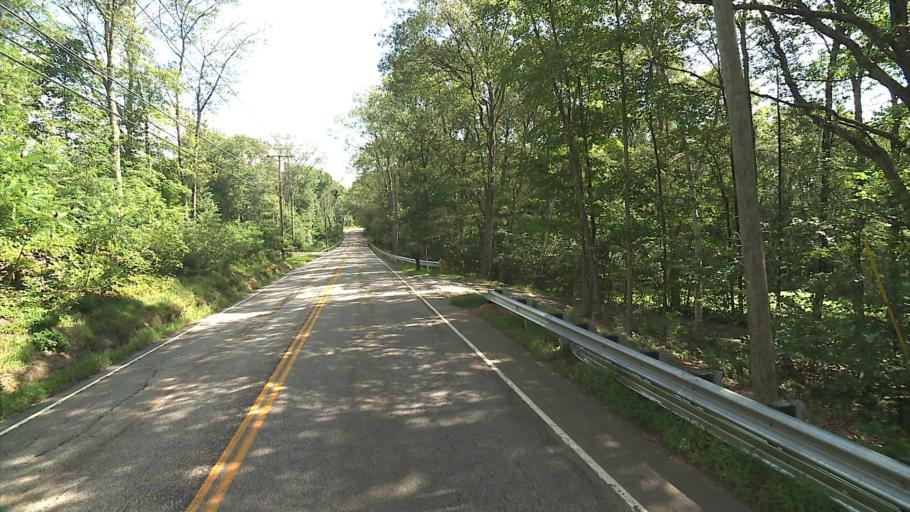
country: US
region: Connecticut
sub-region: Tolland County
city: Stafford
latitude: 41.9715
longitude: -72.1925
